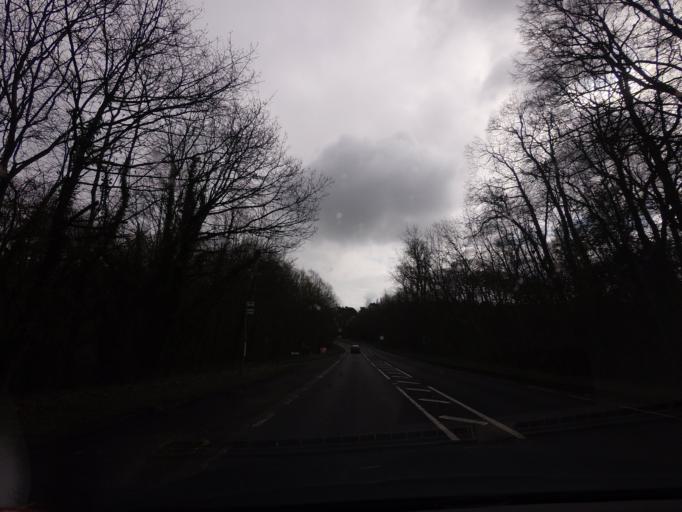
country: GB
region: England
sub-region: Kent
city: Kemsing
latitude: 51.2779
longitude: 0.2622
